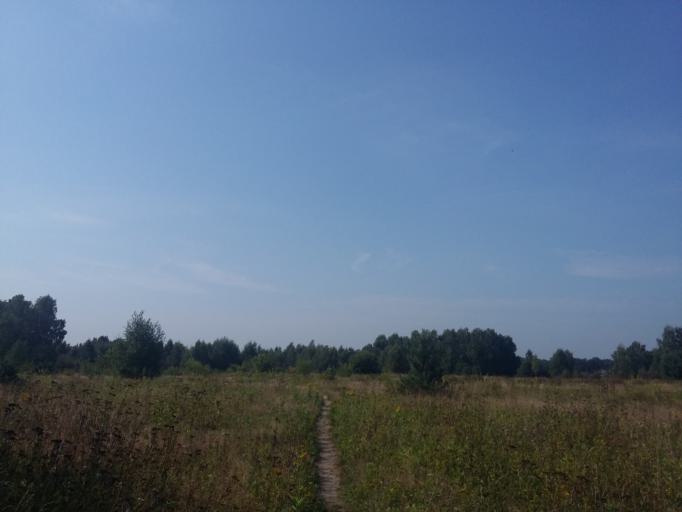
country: PL
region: Lodz Voivodeship
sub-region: Powiat pabianicki
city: Ksawerow
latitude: 51.7321
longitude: 19.3869
